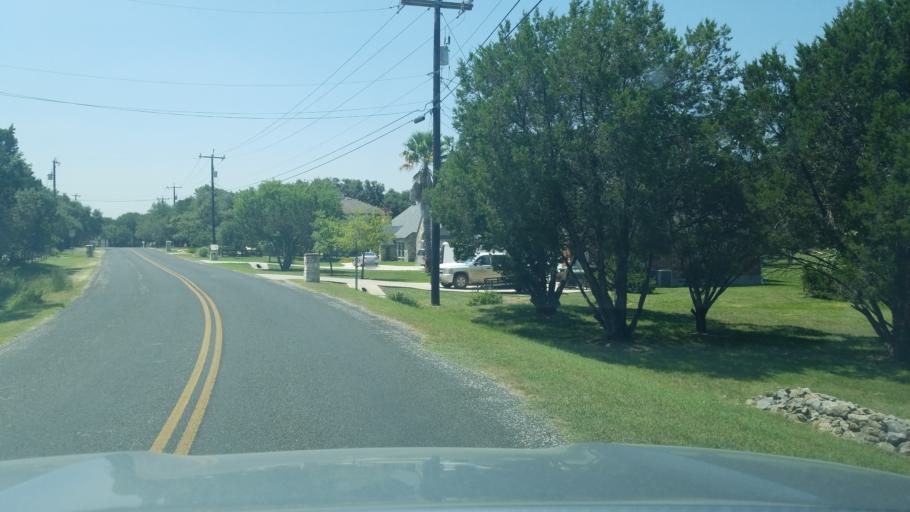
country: US
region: Texas
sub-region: Bexar County
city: Timberwood Park
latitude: 29.6912
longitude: -98.4902
